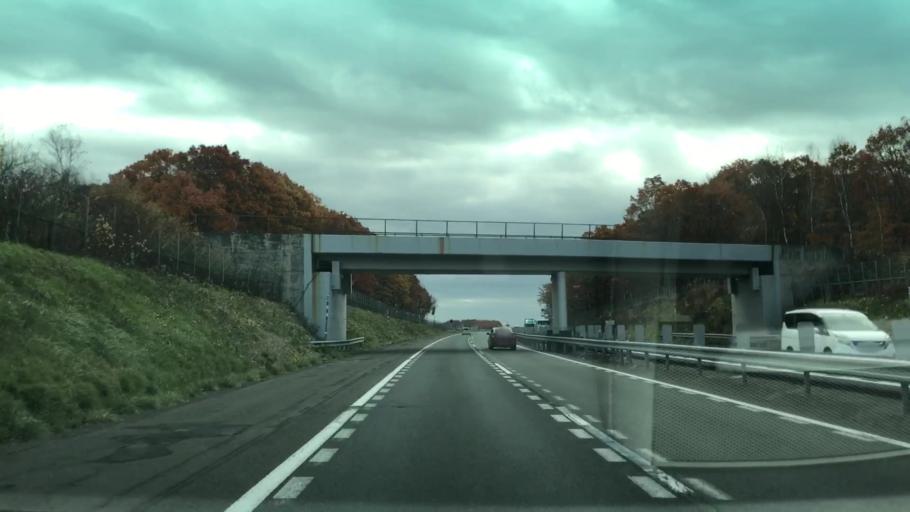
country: JP
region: Hokkaido
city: Kitahiroshima
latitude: 42.9190
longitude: 141.5456
